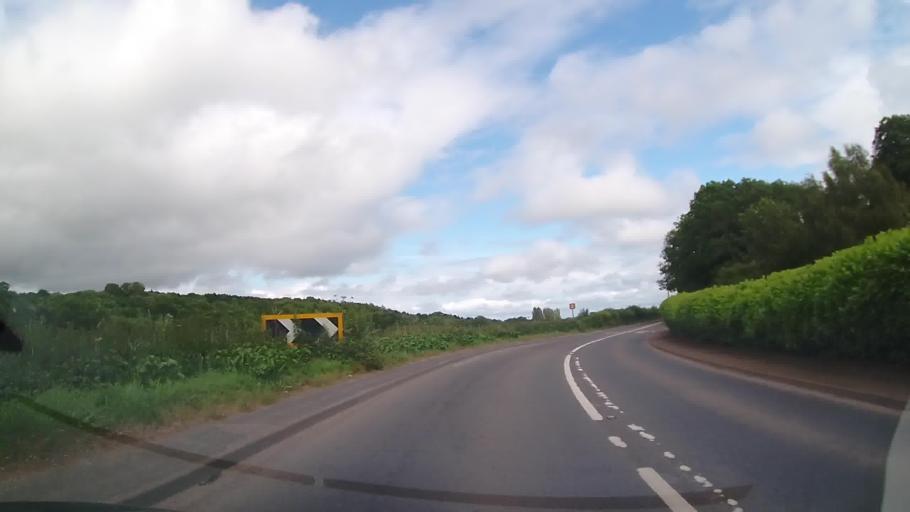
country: GB
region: England
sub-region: Shropshire
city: Pant
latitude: 52.8109
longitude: -3.0802
